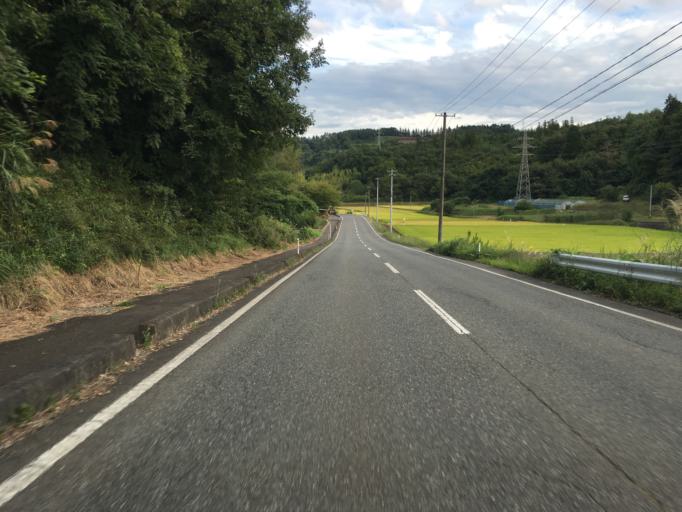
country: JP
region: Fukushima
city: Hobaramachi
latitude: 37.7860
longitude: 140.5449
